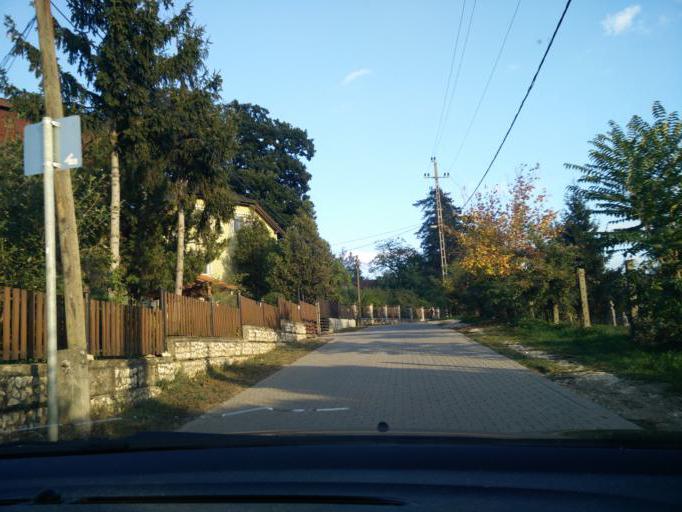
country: HU
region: Pest
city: Piliscsaba
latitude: 47.6351
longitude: 18.8316
